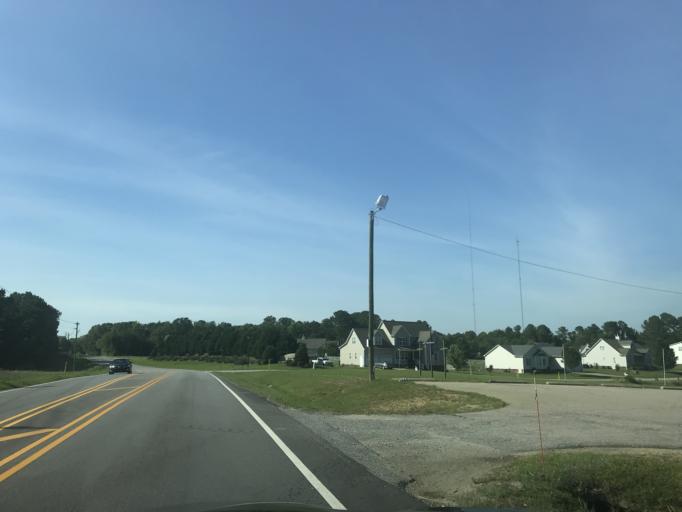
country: US
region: North Carolina
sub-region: Johnston County
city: Clayton
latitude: 35.6506
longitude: -78.5402
